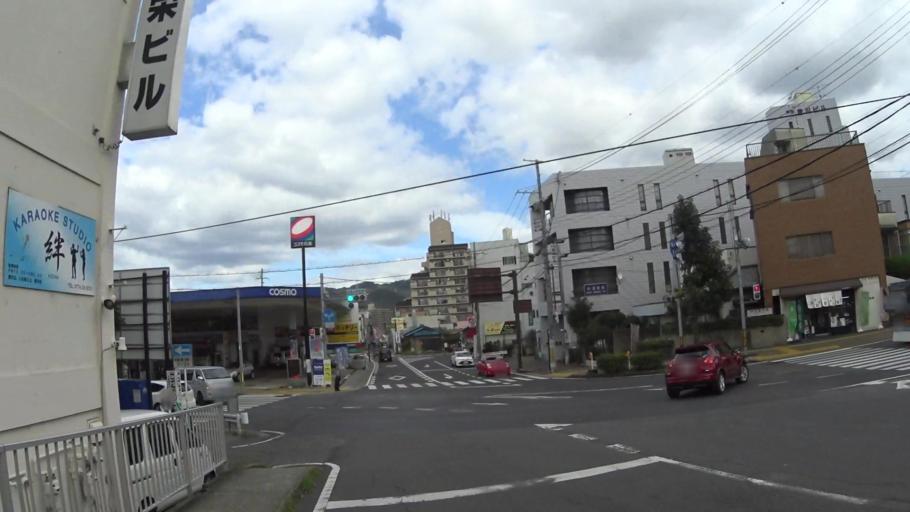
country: JP
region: Kyoto
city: Uji
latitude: 34.8872
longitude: 135.7989
